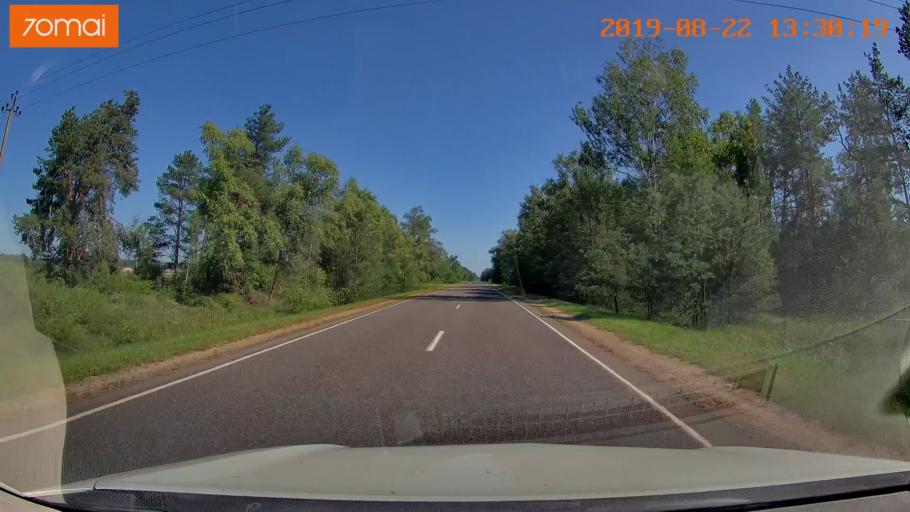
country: BY
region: Minsk
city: Staryya Darohi
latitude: 53.2173
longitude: 28.1534
